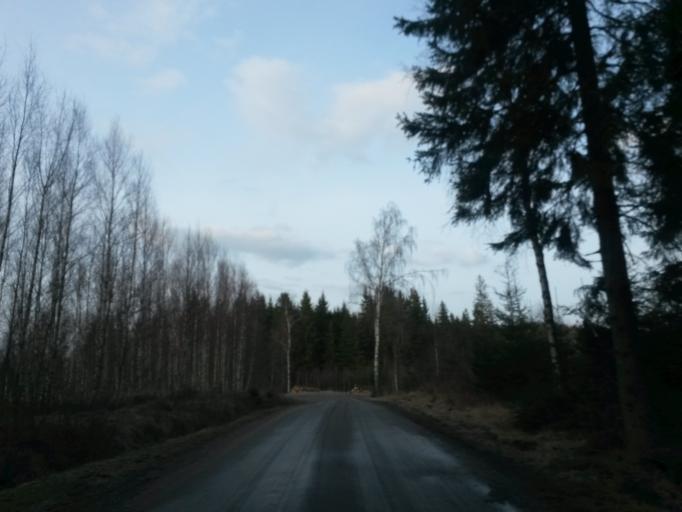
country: SE
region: Vaestra Goetaland
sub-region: Vargarda Kommun
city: Vargarda
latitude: 58.0070
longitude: 12.7716
